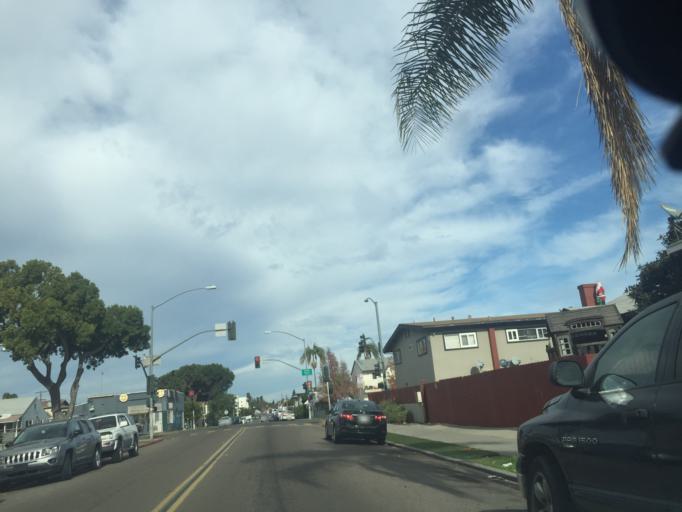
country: US
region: California
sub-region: San Diego County
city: Lemon Grove
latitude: 32.7526
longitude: -117.0923
